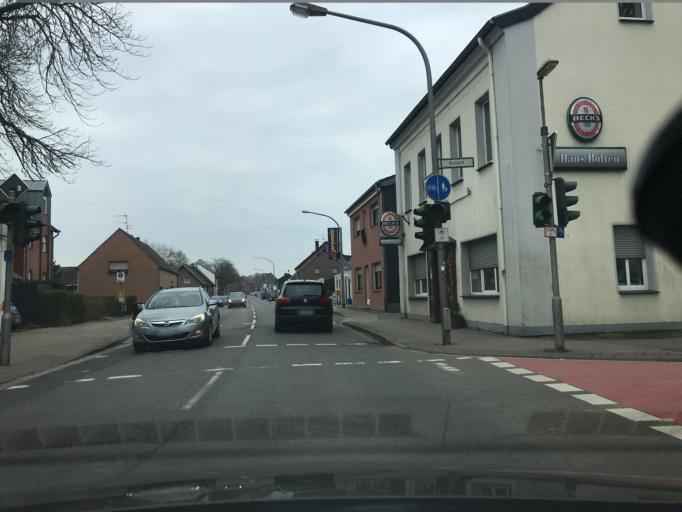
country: DE
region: North Rhine-Westphalia
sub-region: Regierungsbezirk Dusseldorf
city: Viersen
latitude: 51.2684
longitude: 6.3456
